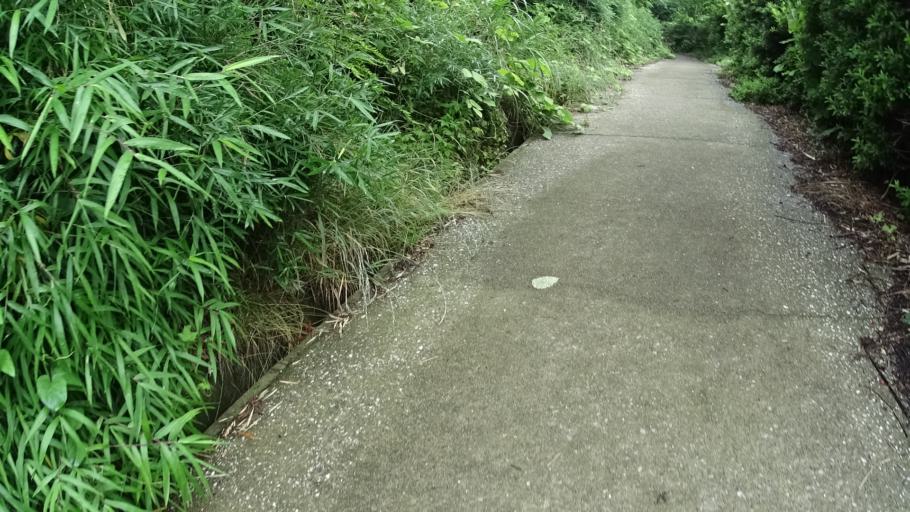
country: JP
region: Kanagawa
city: Zushi
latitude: 35.3549
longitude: 139.6039
